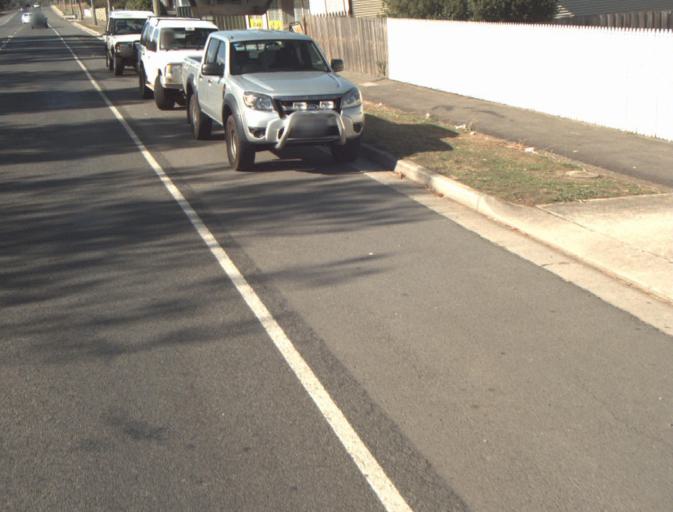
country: AU
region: Tasmania
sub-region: Launceston
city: Mayfield
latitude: -41.3775
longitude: 147.1287
